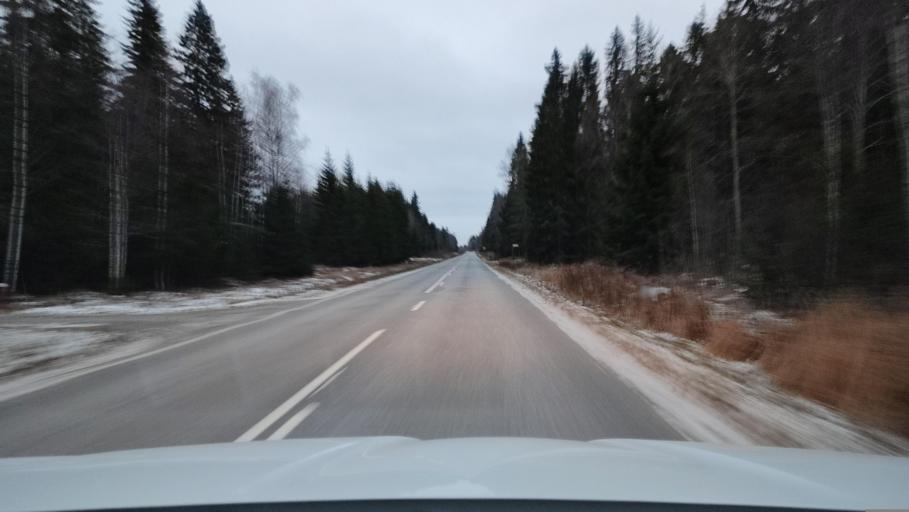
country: FI
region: Ostrobothnia
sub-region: Vaasa
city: Replot
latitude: 63.2384
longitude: 21.3890
